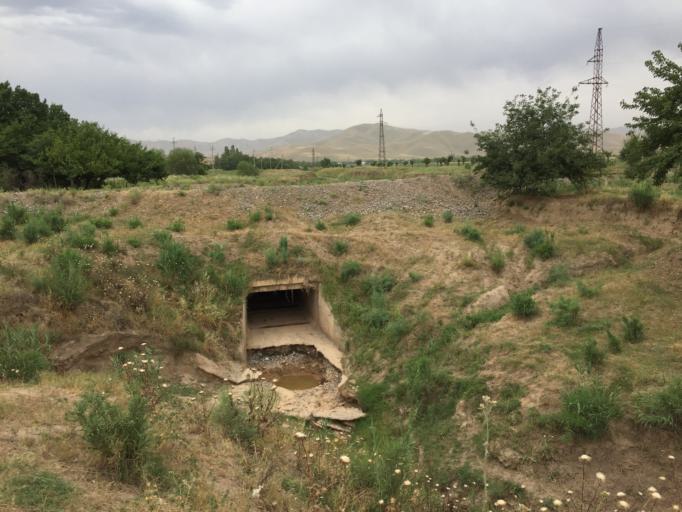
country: TJ
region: Khatlon
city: Kulob
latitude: 37.8443
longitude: 69.7396
